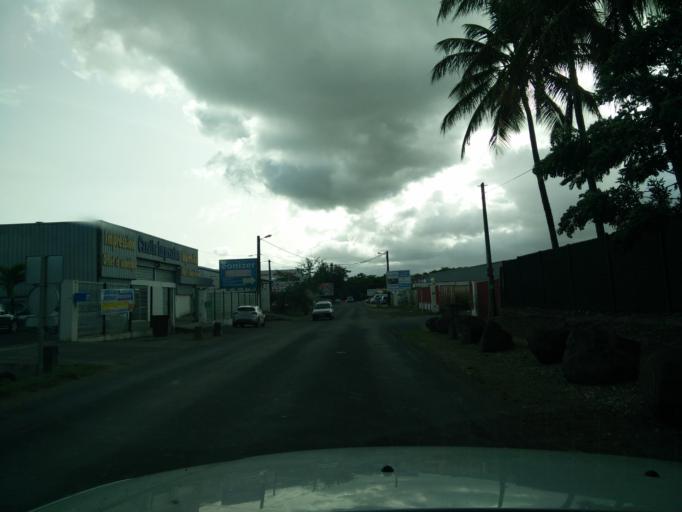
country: GP
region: Guadeloupe
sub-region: Guadeloupe
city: Pointe-a-Pitre
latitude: 16.2459
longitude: -61.5587
